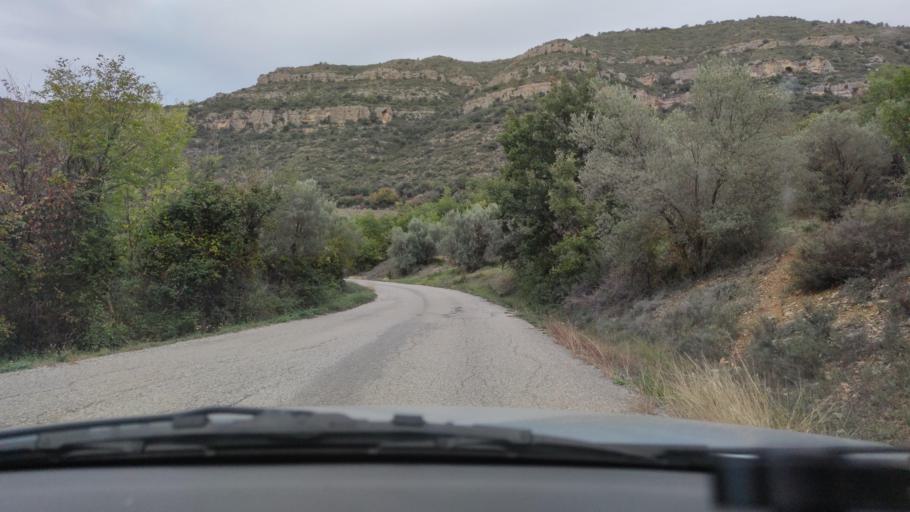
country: ES
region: Catalonia
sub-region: Provincia de Lleida
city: Llimiana
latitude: 42.0683
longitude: 0.9497
